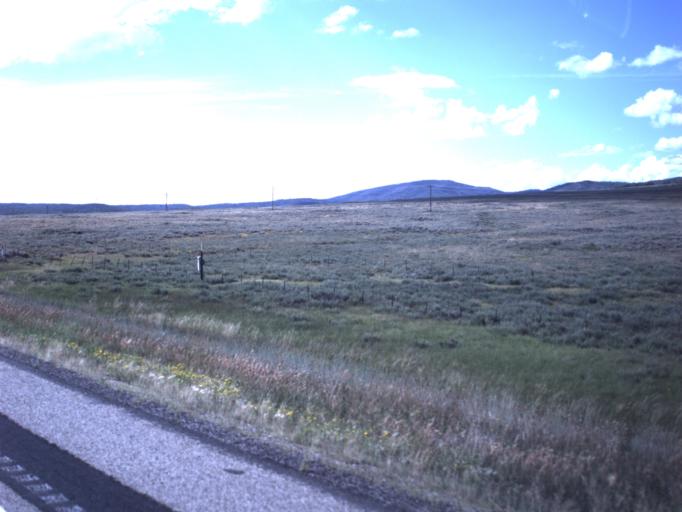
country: US
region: Utah
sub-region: Wasatch County
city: Heber
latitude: 40.2391
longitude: -111.1435
